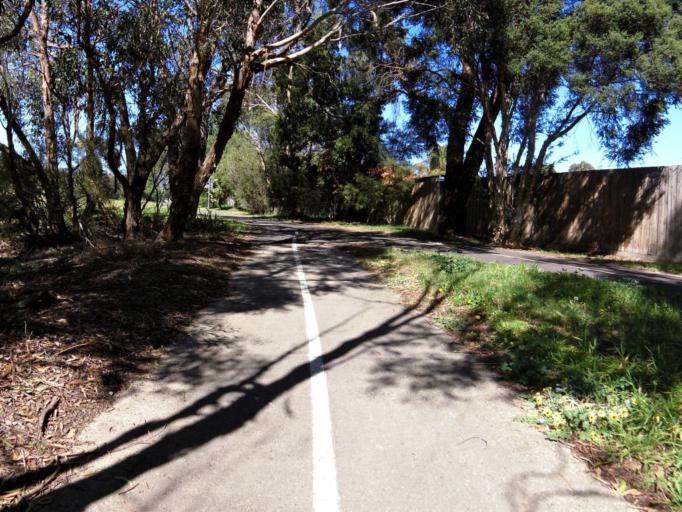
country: AU
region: Victoria
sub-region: Knox
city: Rowville
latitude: -37.9301
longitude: 145.2365
